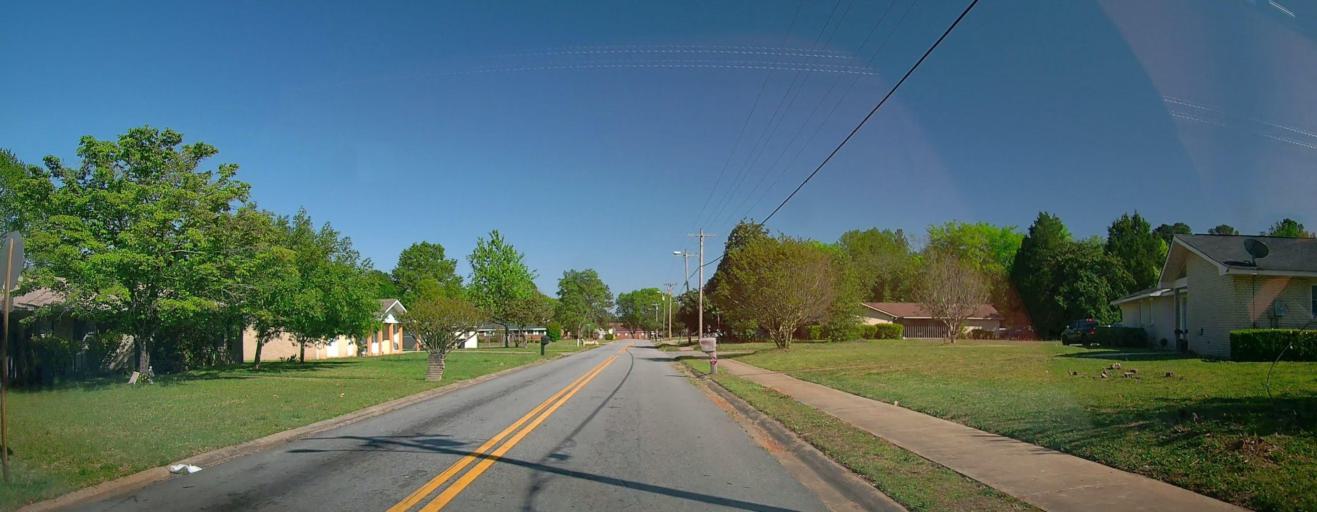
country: US
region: Georgia
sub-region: Houston County
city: Warner Robins
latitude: 32.6400
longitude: -83.6374
